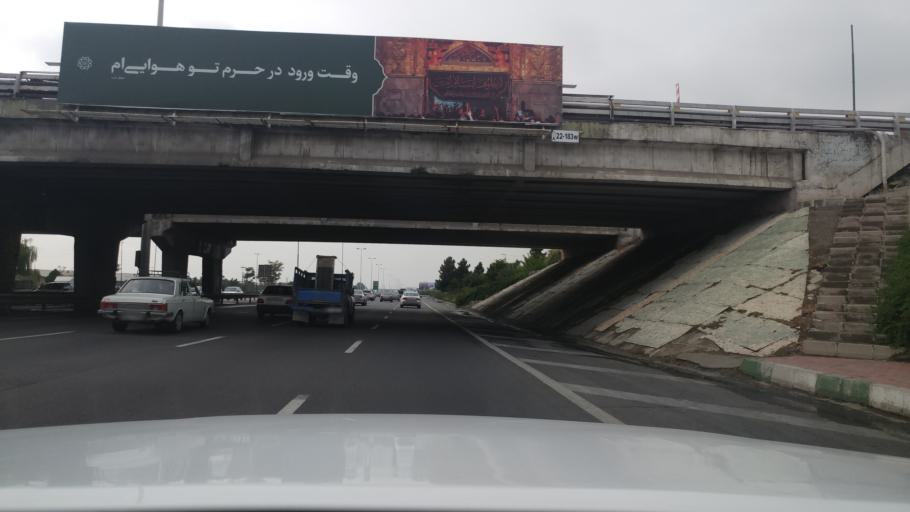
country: IR
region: Tehran
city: Tehran
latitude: 35.7152
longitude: 51.2667
